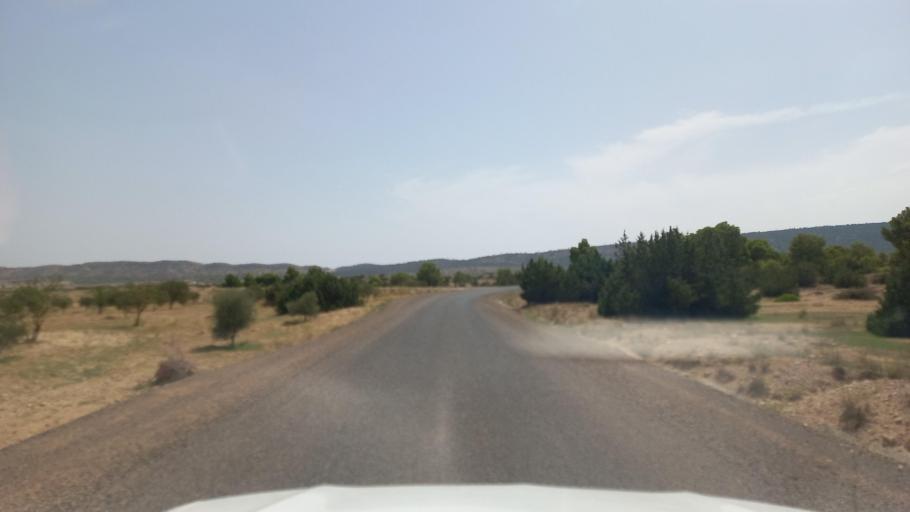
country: TN
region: Al Qasrayn
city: Sbiba
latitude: 35.3937
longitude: 8.9489
